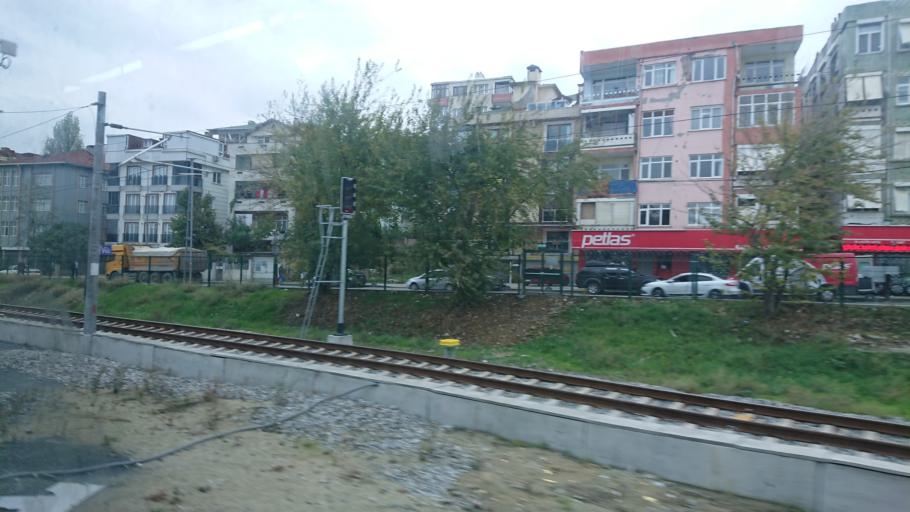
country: TR
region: Istanbul
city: Mahmutbey
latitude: 41.0073
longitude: 28.7745
